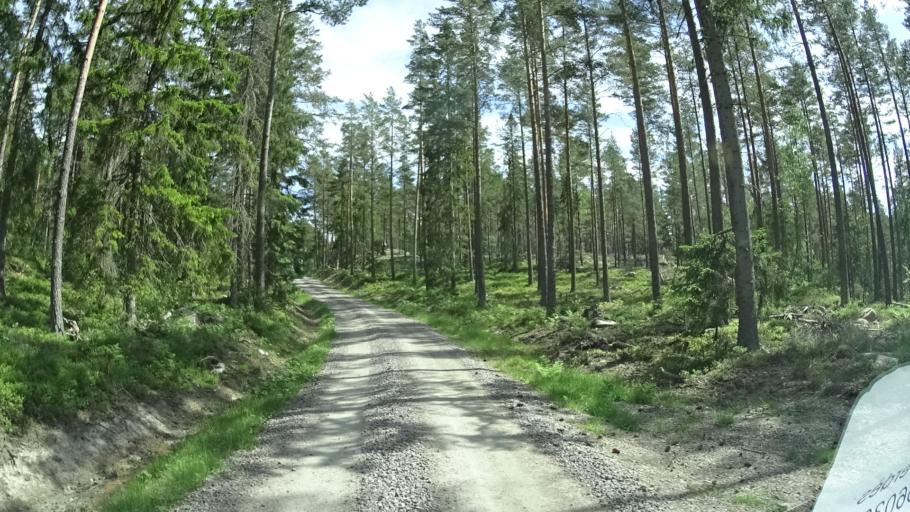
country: SE
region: OEstergoetland
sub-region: Norrkopings Kommun
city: Svartinge
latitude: 58.7709
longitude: 15.9473
